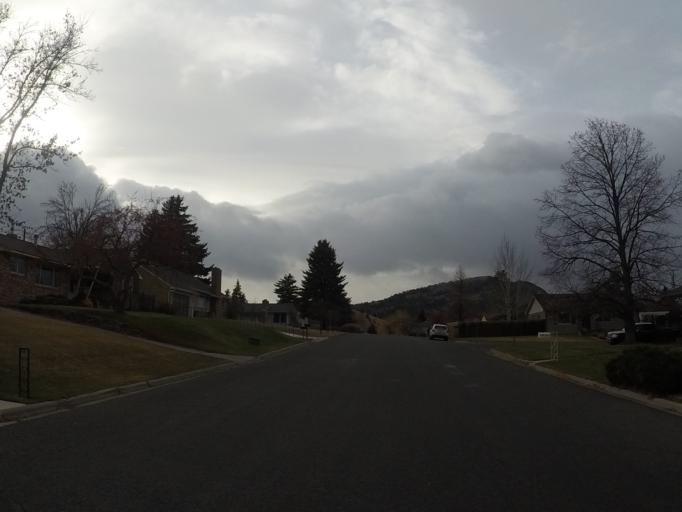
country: US
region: Montana
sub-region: Lewis and Clark County
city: Helena
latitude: 46.5831
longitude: -112.0177
